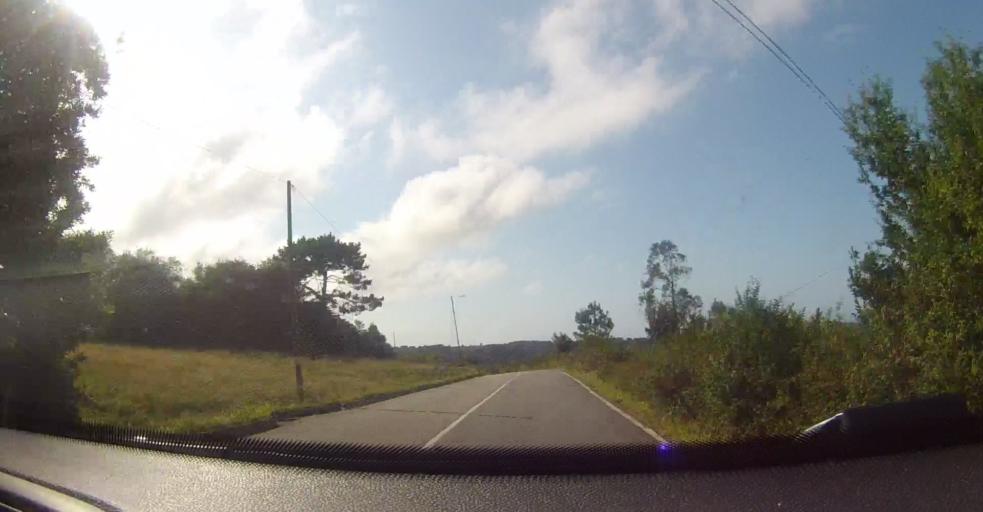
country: ES
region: Asturias
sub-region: Province of Asturias
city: Villaviciosa
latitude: 43.5399
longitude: -5.3960
